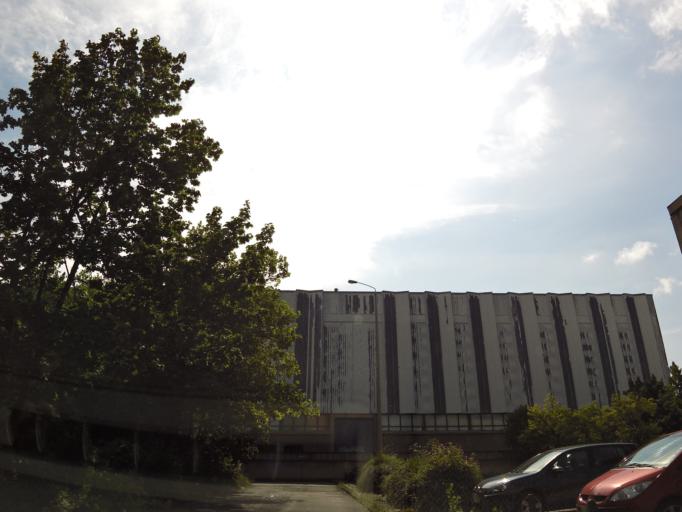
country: DE
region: Saxony
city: Leipzig
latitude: 51.3213
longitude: 12.3984
